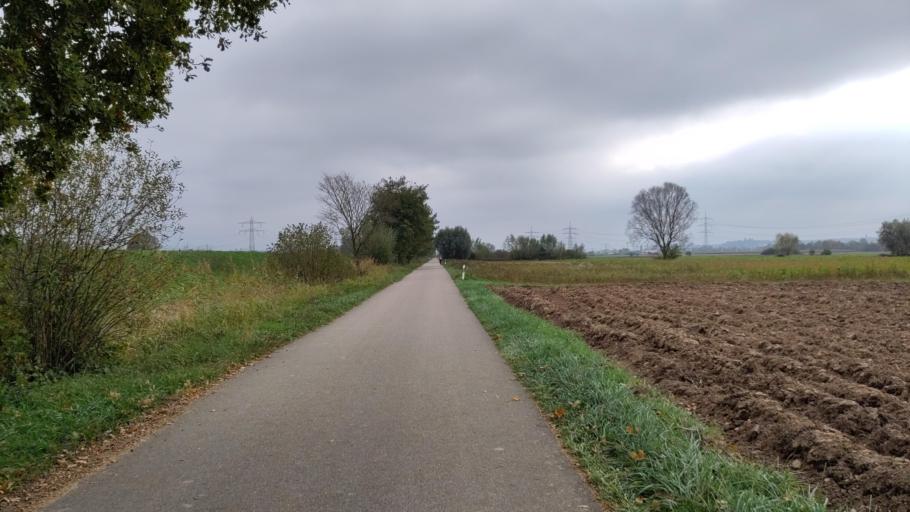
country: DE
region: Baden-Wuerttemberg
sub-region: Freiburg Region
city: Riegel
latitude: 48.1417
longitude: 7.7554
